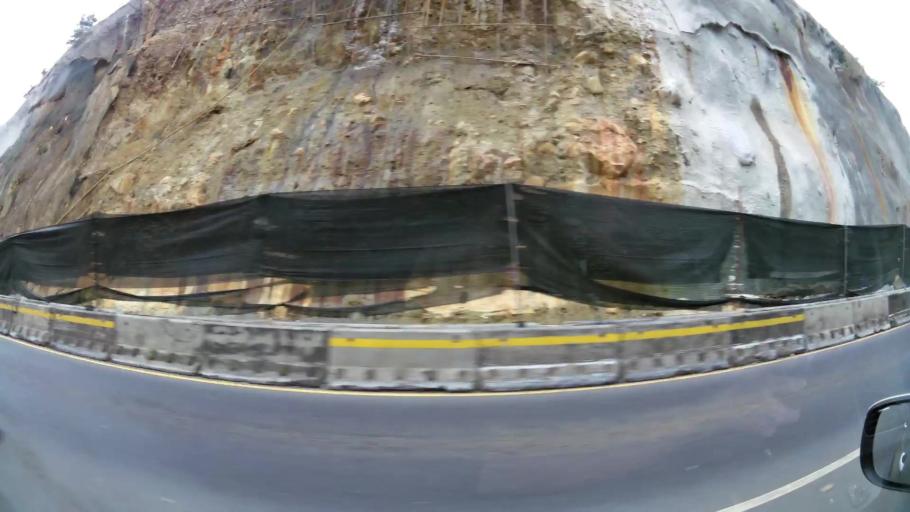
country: CR
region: Alajuela
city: Atenas
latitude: 9.9350
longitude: -84.4076
